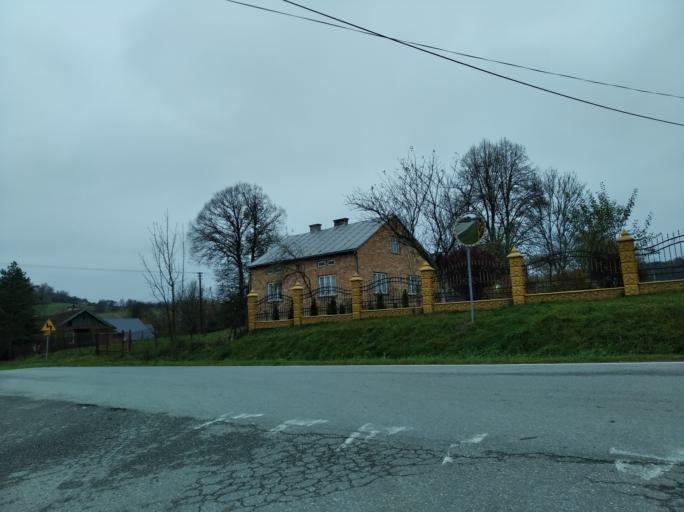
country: PL
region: Subcarpathian Voivodeship
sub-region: Powiat krosnienski
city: Leki
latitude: 49.8028
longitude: 21.6710
